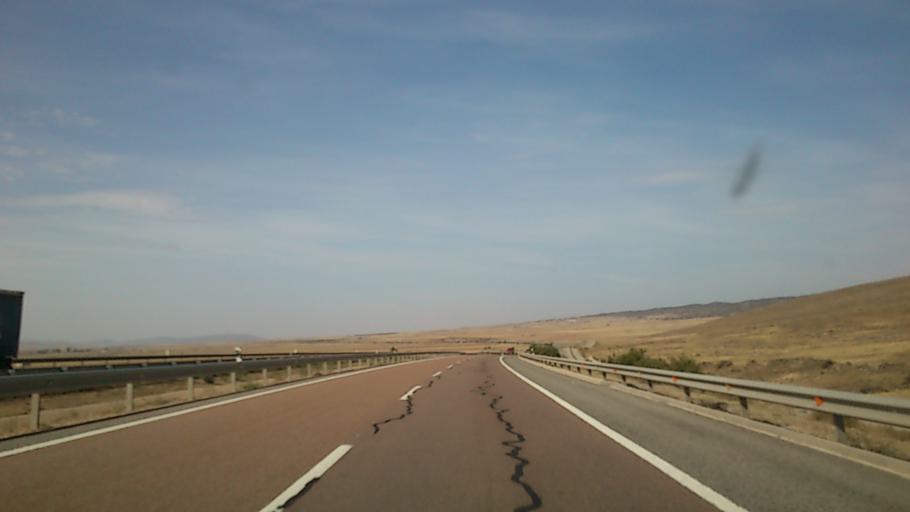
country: ES
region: Aragon
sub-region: Provincia de Teruel
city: Singra
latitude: 40.6581
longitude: -1.3180
